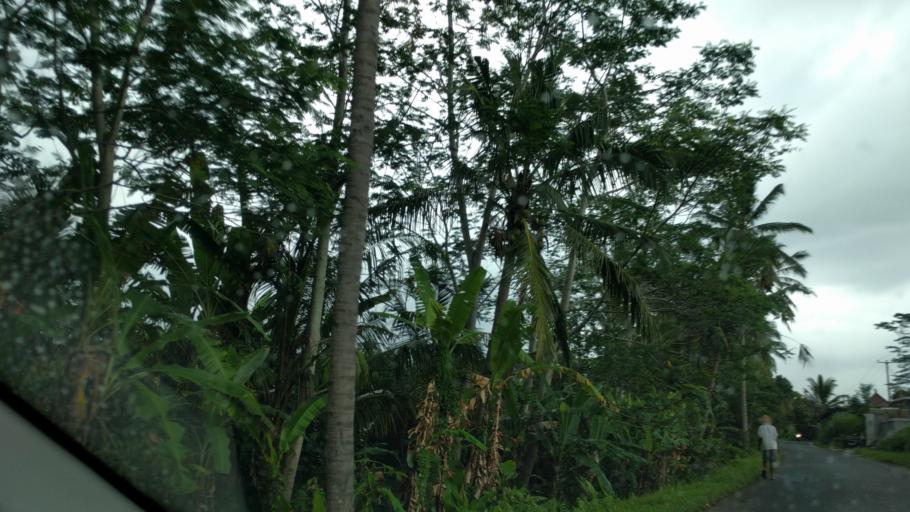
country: ID
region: Bali
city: Banjar Triwangsakeliki
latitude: -8.4589
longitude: 115.2597
